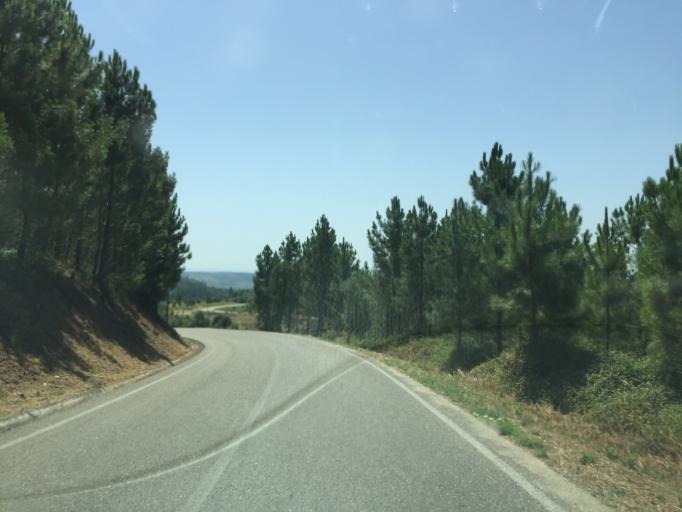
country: PT
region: Santarem
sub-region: Ferreira do Zezere
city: Ferreira do Zezere
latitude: 39.5972
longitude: -8.3010
